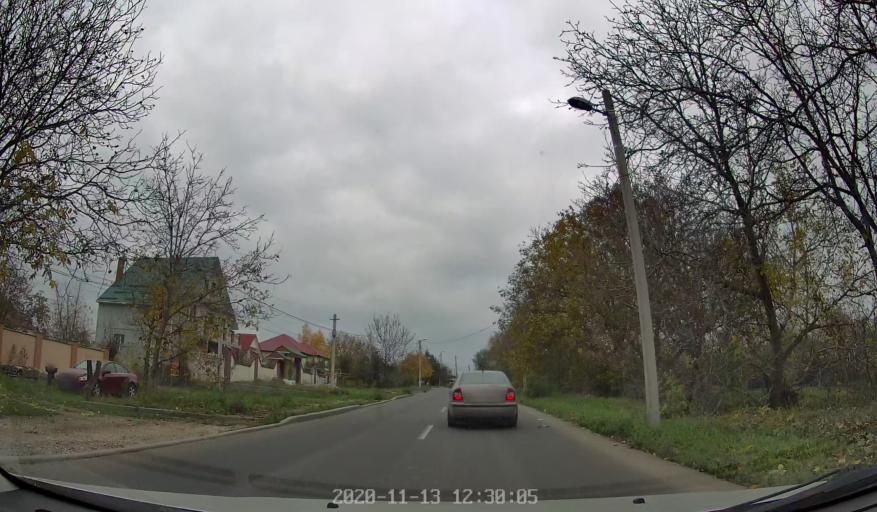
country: MD
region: Chisinau
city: Chisinau
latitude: 46.9668
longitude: 28.8341
